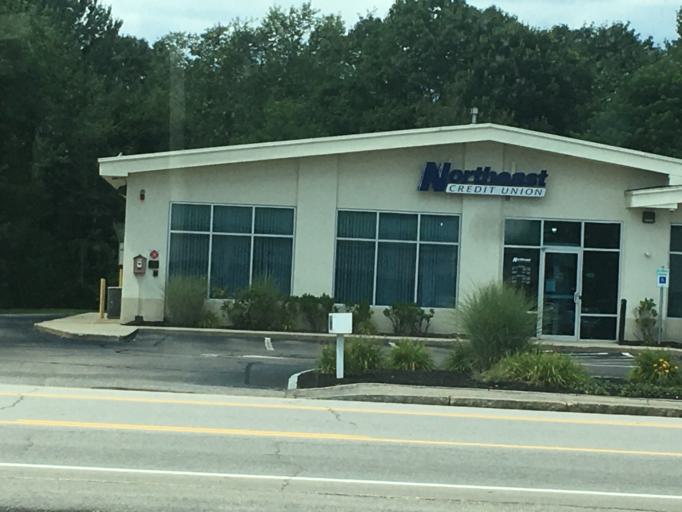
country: US
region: New Hampshire
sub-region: Rockingham County
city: Exeter
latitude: 42.9861
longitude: -70.9360
